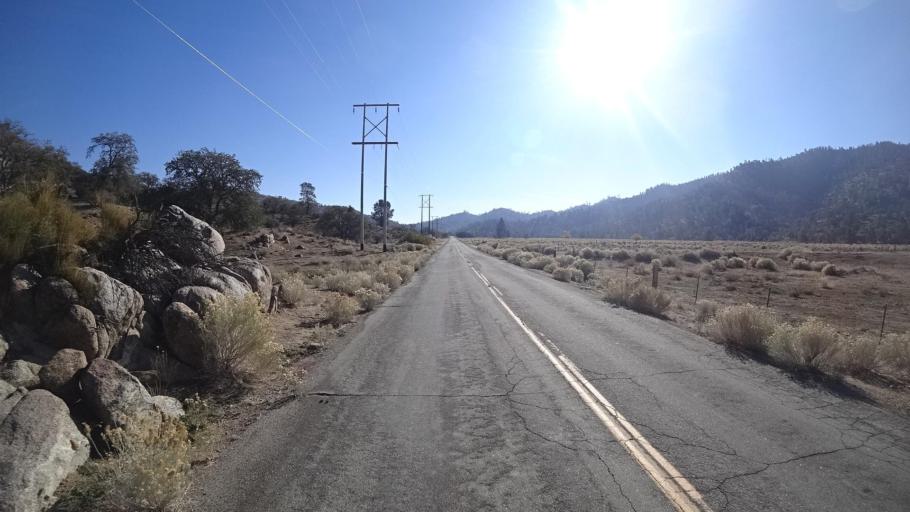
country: US
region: California
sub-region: Kern County
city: Bodfish
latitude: 35.3936
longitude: -118.4348
